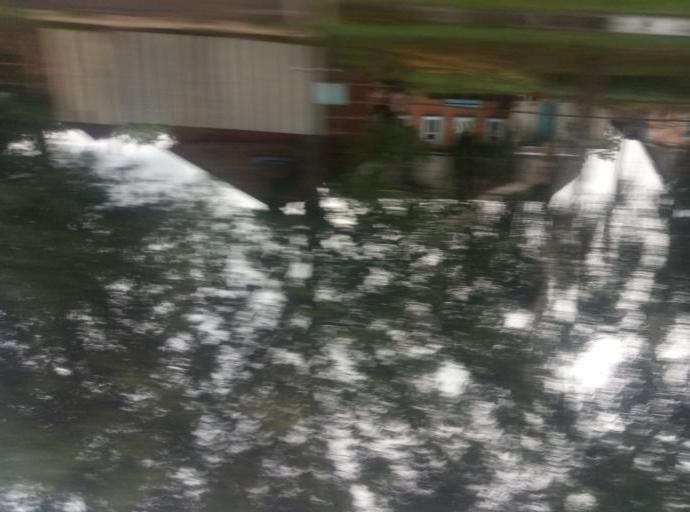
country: RU
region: Tula
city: Kireyevsk
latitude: 53.9917
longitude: 37.9277
